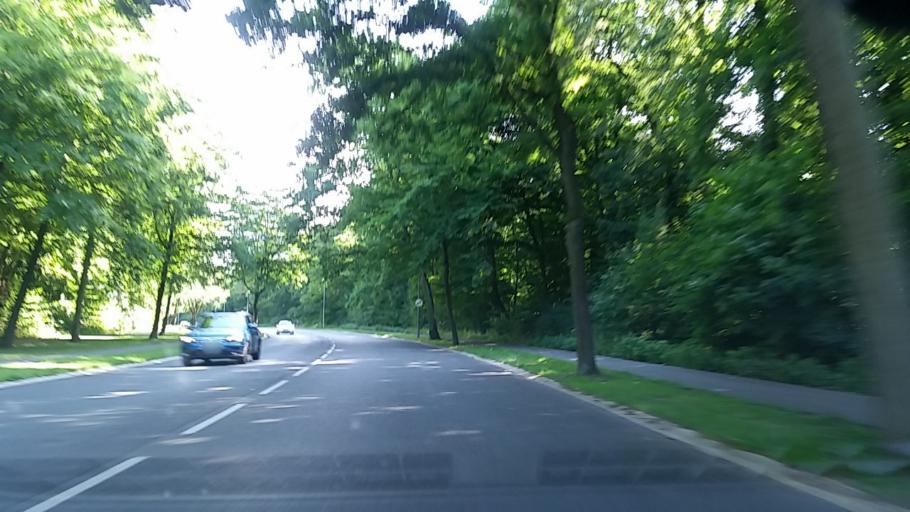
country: DE
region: Lower Saxony
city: Wolfsburg
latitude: 52.4169
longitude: 10.7604
